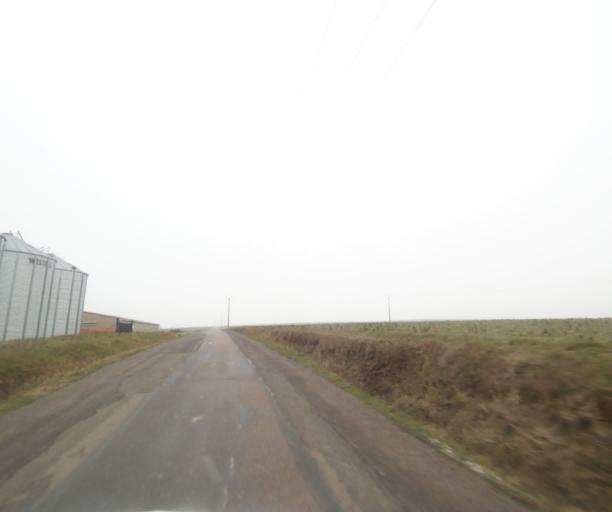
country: FR
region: Champagne-Ardenne
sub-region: Departement de la Haute-Marne
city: Bienville
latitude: 48.5439
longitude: 5.0689
